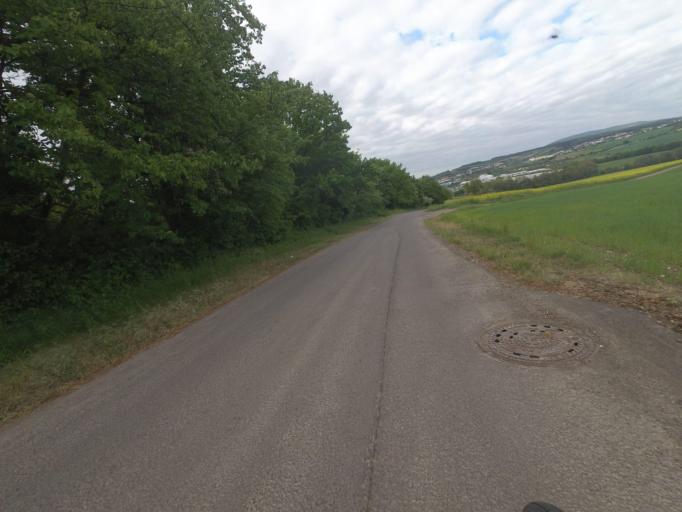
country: DE
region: Rheinland-Pfalz
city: Morschheim
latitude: 49.6853
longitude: 8.0201
